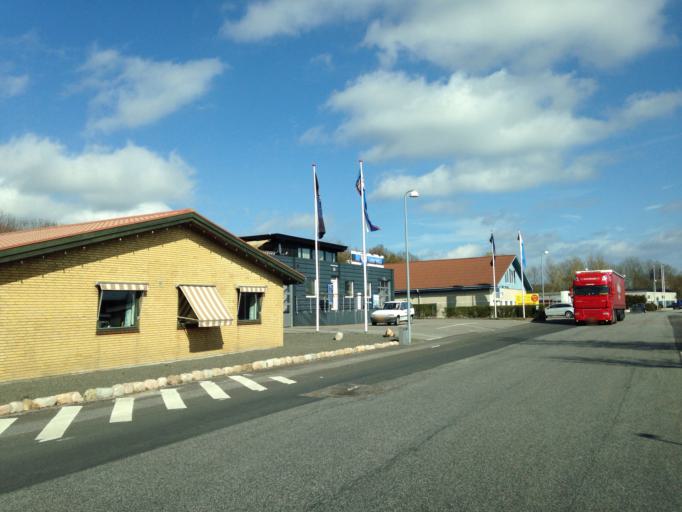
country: DK
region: Zealand
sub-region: Greve Kommune
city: Greve
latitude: 55.5913
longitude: 12.2949
